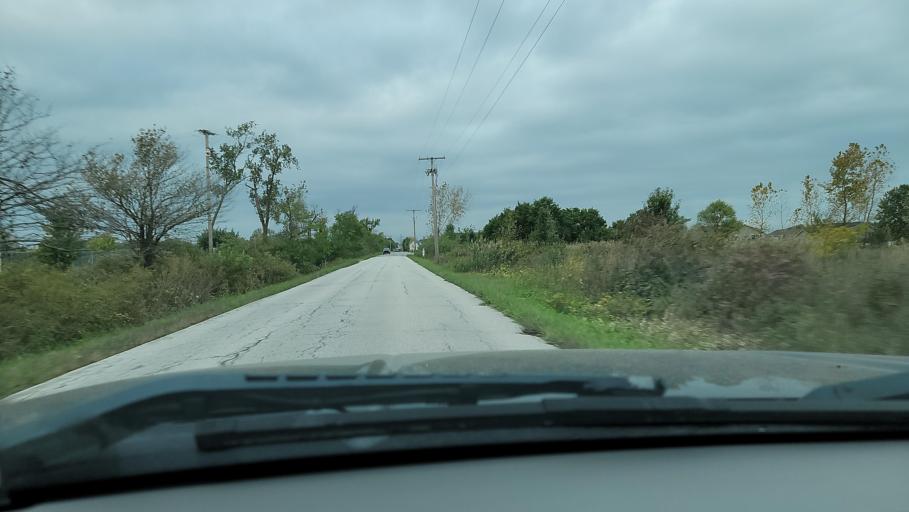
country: US
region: Indiana
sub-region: Porter County
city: Portage
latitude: 41.5614
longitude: -87.1567
